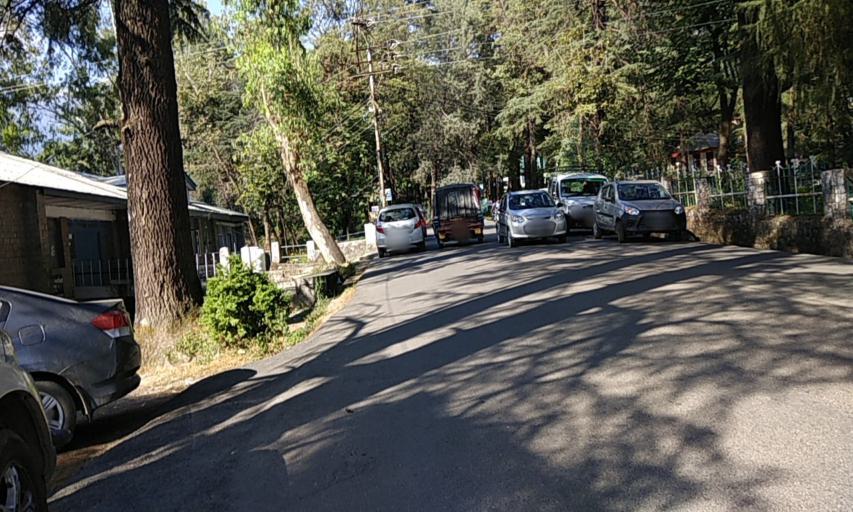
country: IN
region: Himachal Pradesh
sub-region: Kangra
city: Palampur
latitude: 32.1132
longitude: 76.5366
